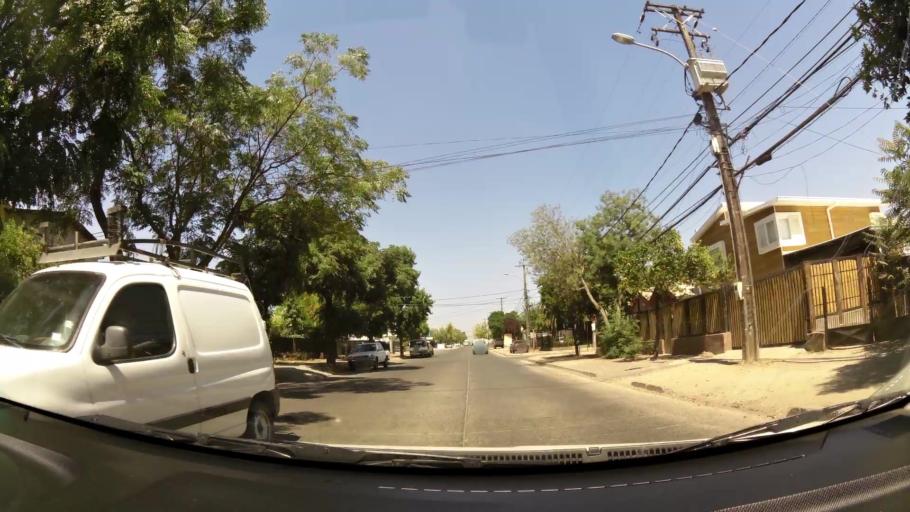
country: CL
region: Maule
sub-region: Provincia de Talca
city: Talca
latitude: -35.4274
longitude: -71.6318
